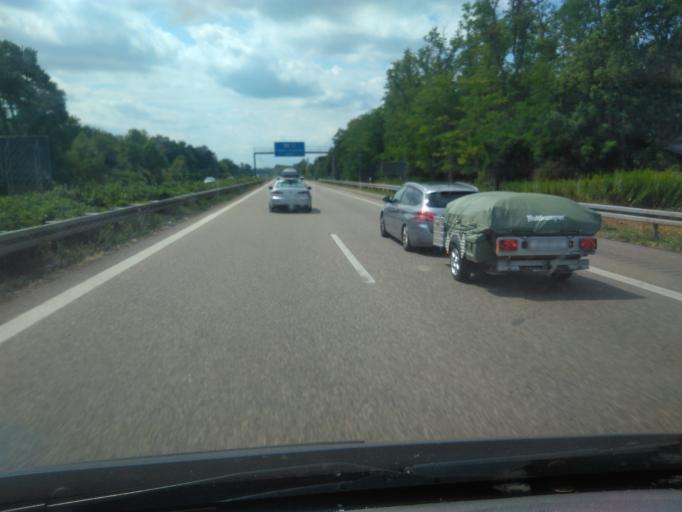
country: FR
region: Alsace
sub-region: Departement du Haut-Rhin
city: Chalampe
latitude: 47.7992
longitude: 7.5429
